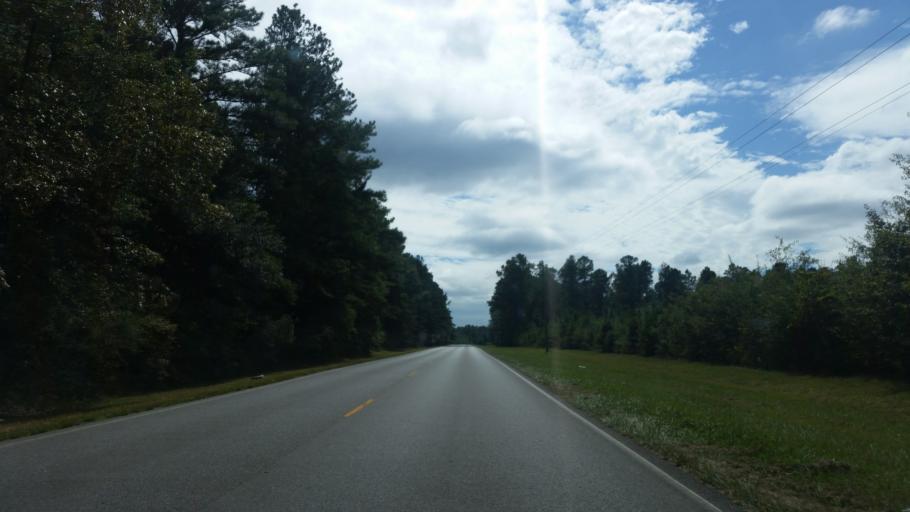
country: US
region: Florida
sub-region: Santa Rosa County
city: Point Baker
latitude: 30.7553
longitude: -86.9431
